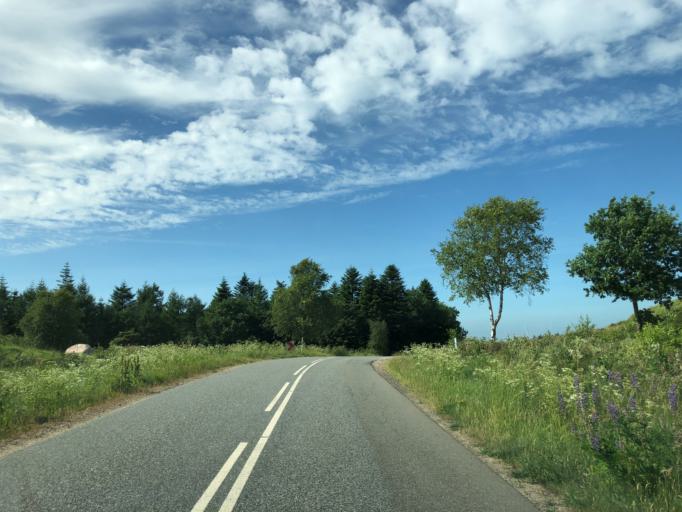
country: DK
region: Central Jutland
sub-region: Herning Kommune
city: Kibaek
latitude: 56.0628
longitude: 8.9169
